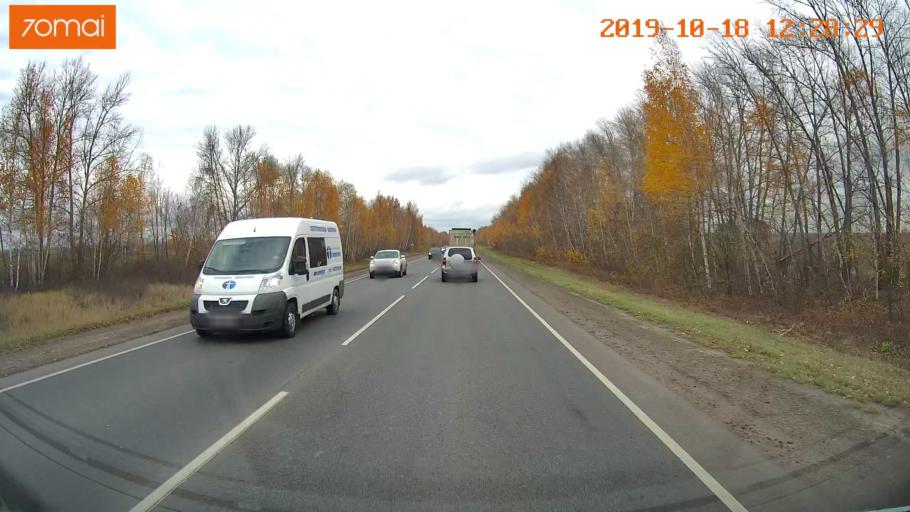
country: RU
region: Rjazan
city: Ryazan'
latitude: 54.5723
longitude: 39.5693
